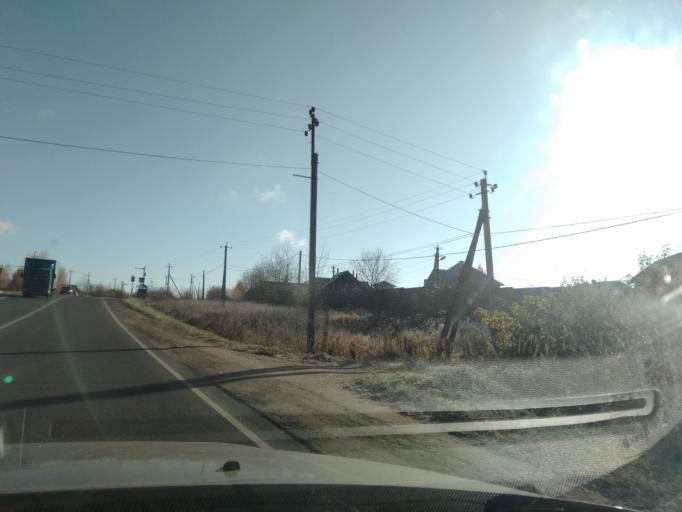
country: RU
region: Moskovskaya
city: Istra
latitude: 55.8815
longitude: 36.8148
